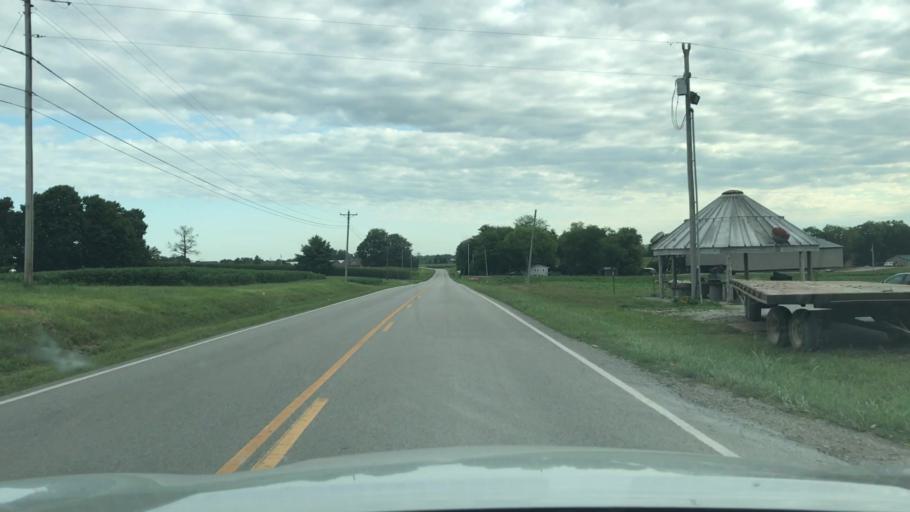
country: US
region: Kentucky
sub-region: Todd County
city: Elkton
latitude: 36.7734
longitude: -87.1660
